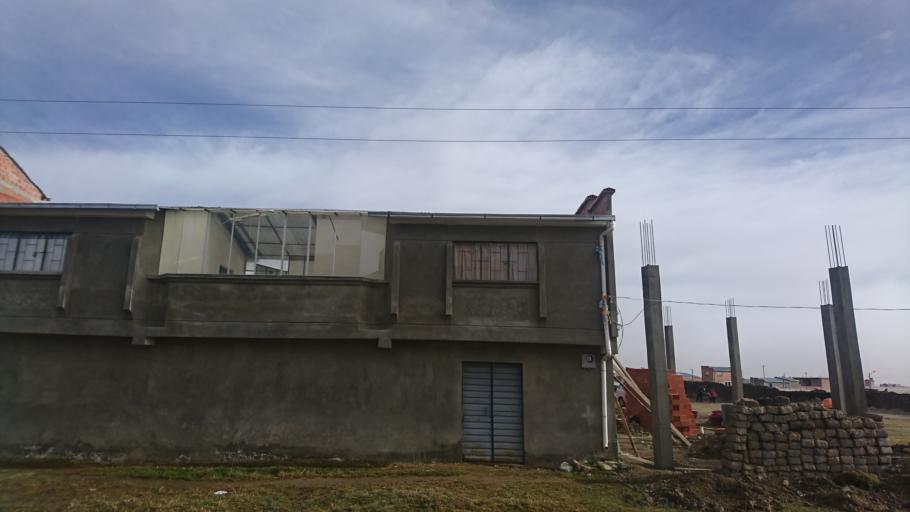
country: BO
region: La Paz
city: Batallas
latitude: -16.3992
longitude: -68.4725
